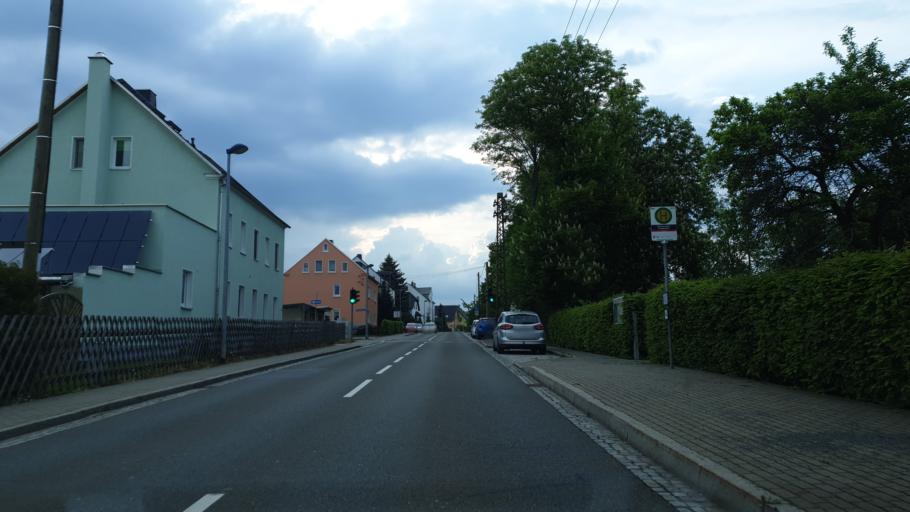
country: DE
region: Saxony
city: Lugau
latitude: 50.7094
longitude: 12.7338
